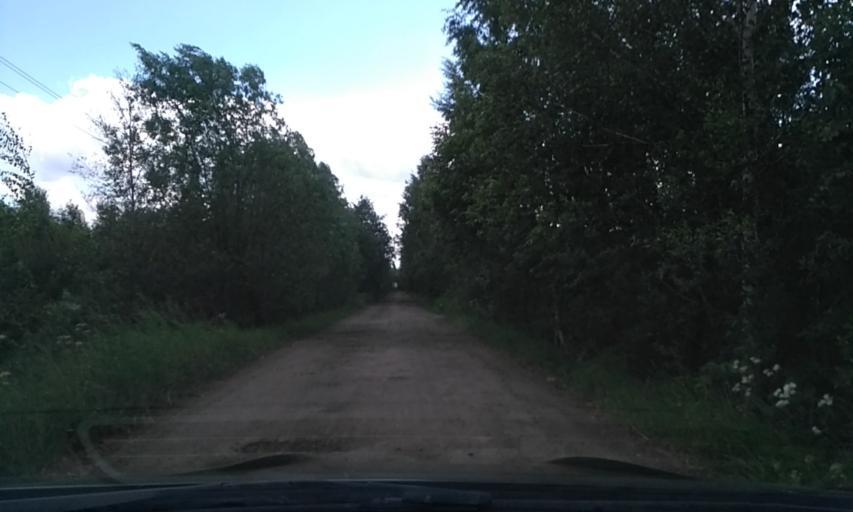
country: RU
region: Leningrad
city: Otradnoye
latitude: 59.8120
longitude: 30.8266
